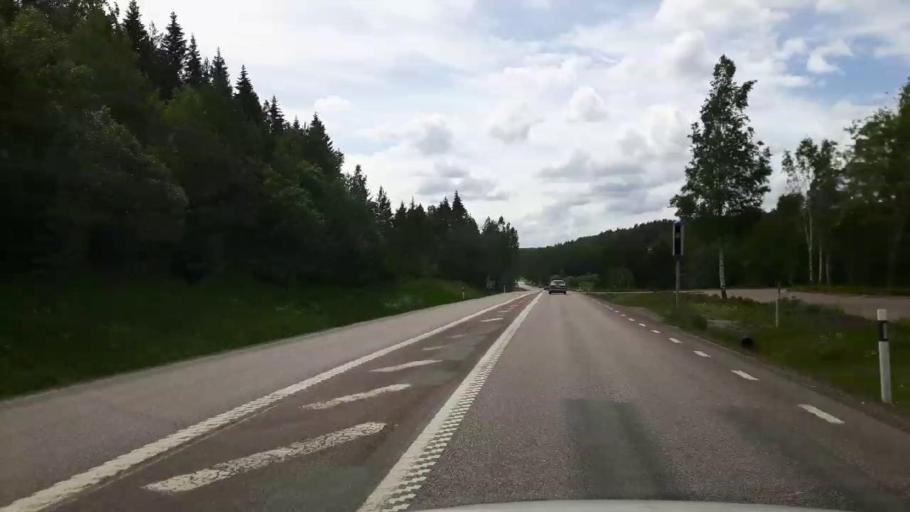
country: SE
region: Vaestmanland
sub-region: Fagersta Kommun
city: Fagersta
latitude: 59.9749
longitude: 15.7864
